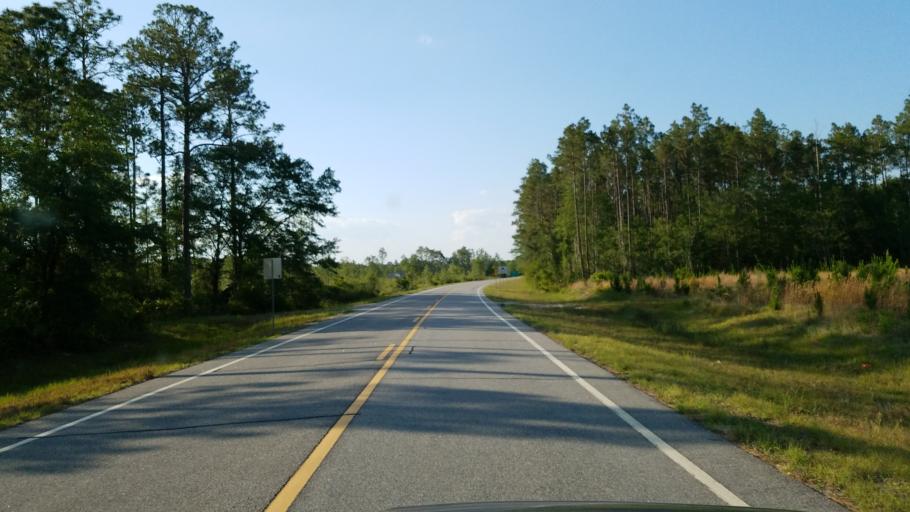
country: US
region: Georgia
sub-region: Echols County
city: Statenville
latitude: 30.8477
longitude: -83.0529
